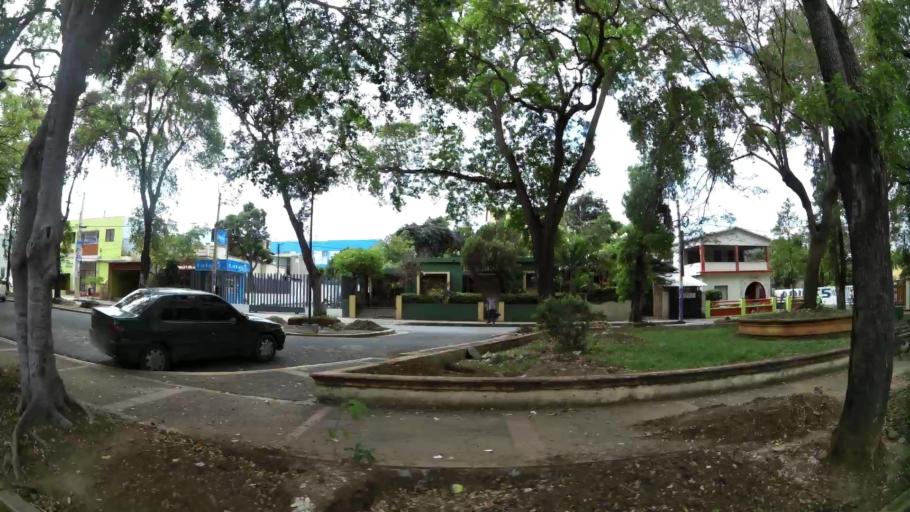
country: DO
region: Santiago
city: Santiago de los Caballeros
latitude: 19.4562
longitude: -70.7102
